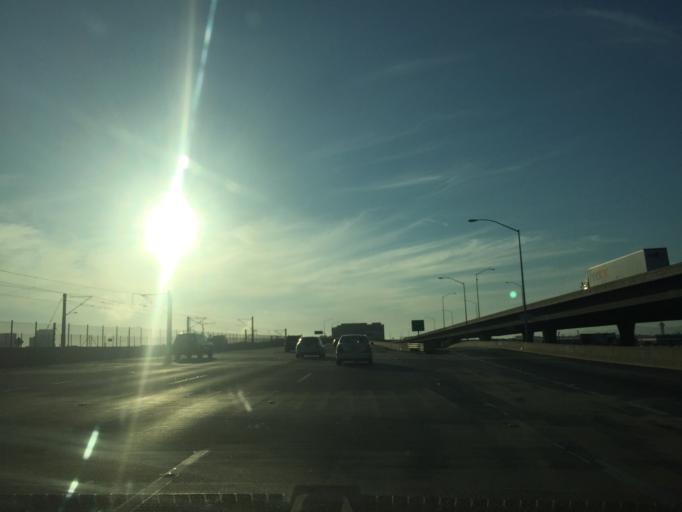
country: US
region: California
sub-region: Los Angeles County
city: Del Aire
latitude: 33.9303
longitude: -118.3701
